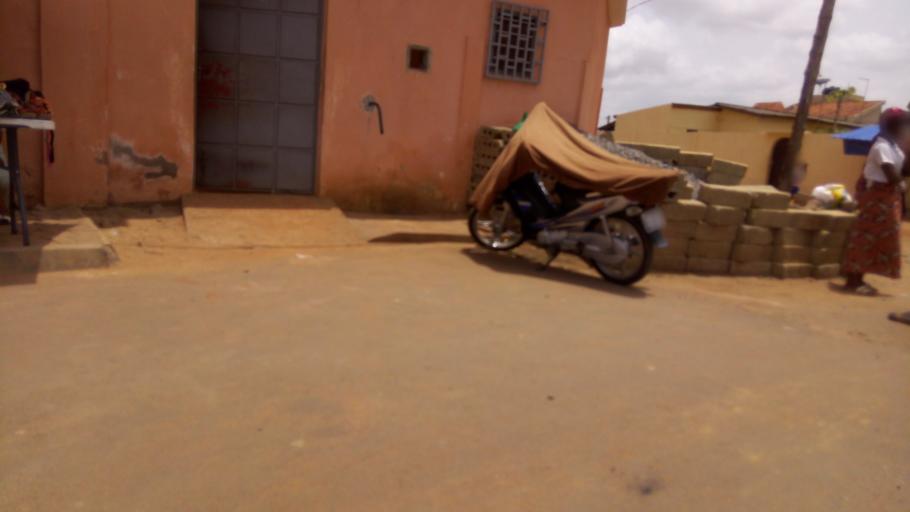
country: TG
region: Maritime
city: Lome
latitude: 6.2130
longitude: 1.1875
